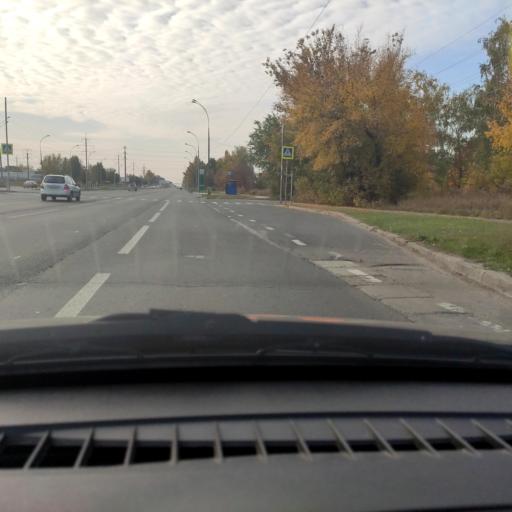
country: RU
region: Samara
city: Tol'yatti
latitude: 53.5516
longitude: 49.2870
